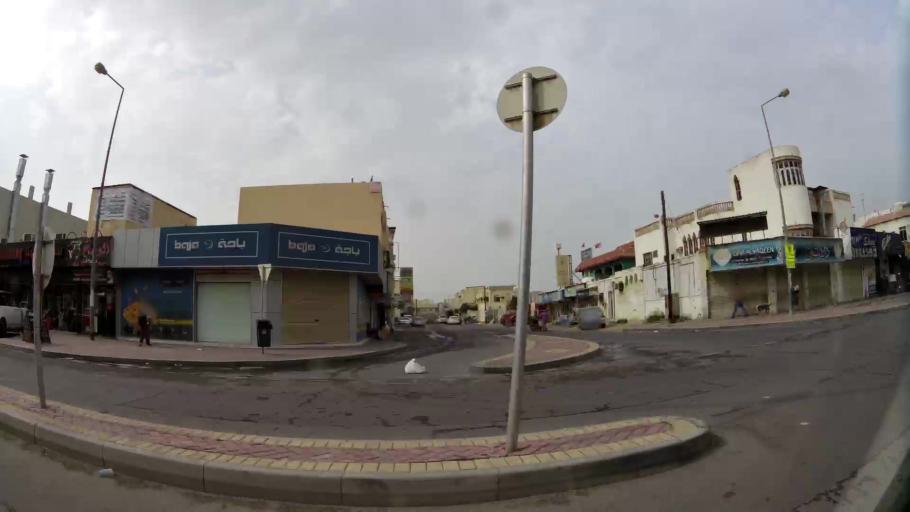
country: BH
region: Northern
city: Ar Rifa'
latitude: 26.1317
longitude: 50.5594
